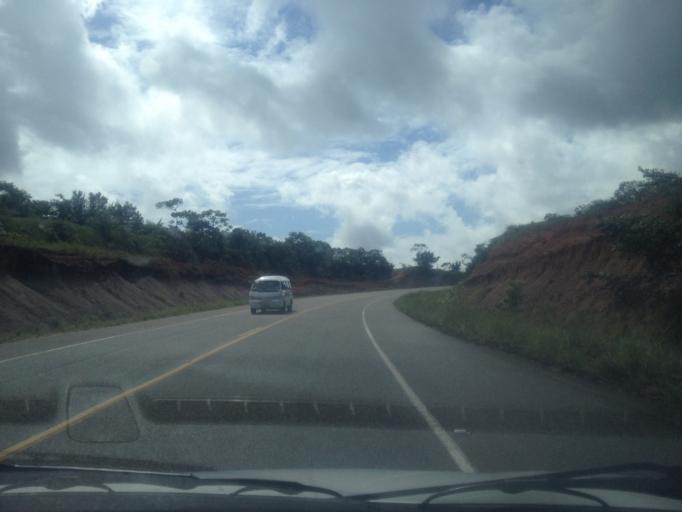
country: BR
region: Bahia
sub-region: Conde
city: Conde
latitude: -12.0557
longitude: -37.7419
